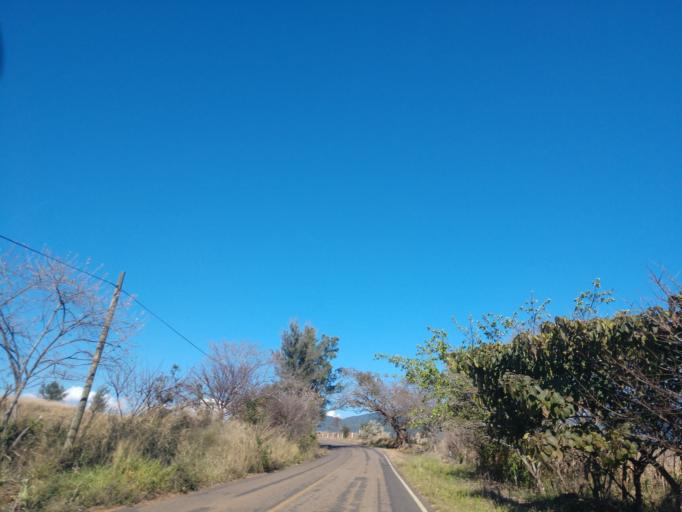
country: MX
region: Nayarit
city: Compostela
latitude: 21.2625
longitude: -104.8948
